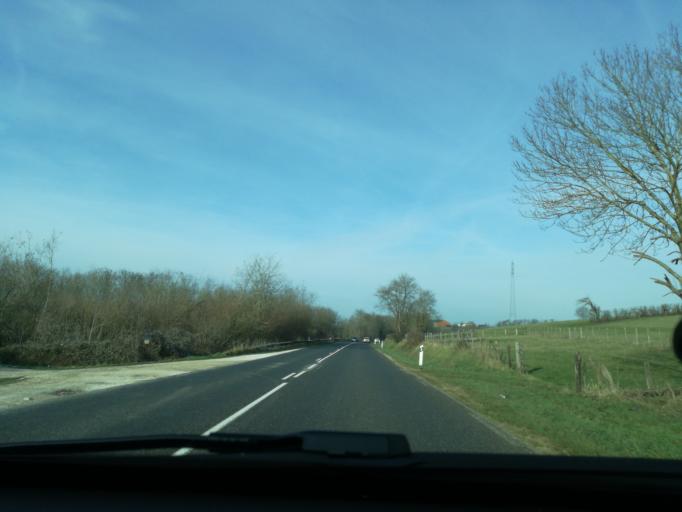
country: FR
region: Lorraine
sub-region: Departement de la Meuse
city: Fains-Veel
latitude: 48.8034
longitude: 5.1165
